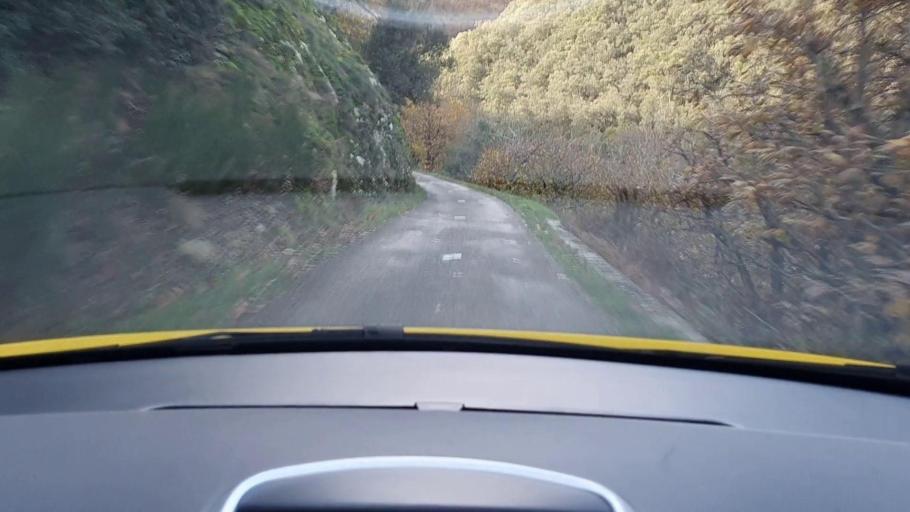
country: FR
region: Languedoc-Roussillon
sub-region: Departement du Gard
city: Valleraugue
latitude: 44.0969
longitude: 3.7337
